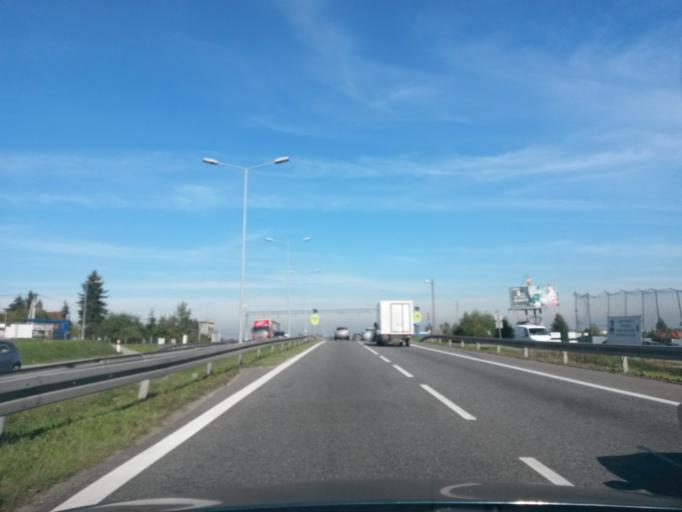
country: PL
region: Lesser Poland Voivodeship
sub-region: Powiat krakowski
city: Libertow
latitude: 49.9729
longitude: 19.9070
